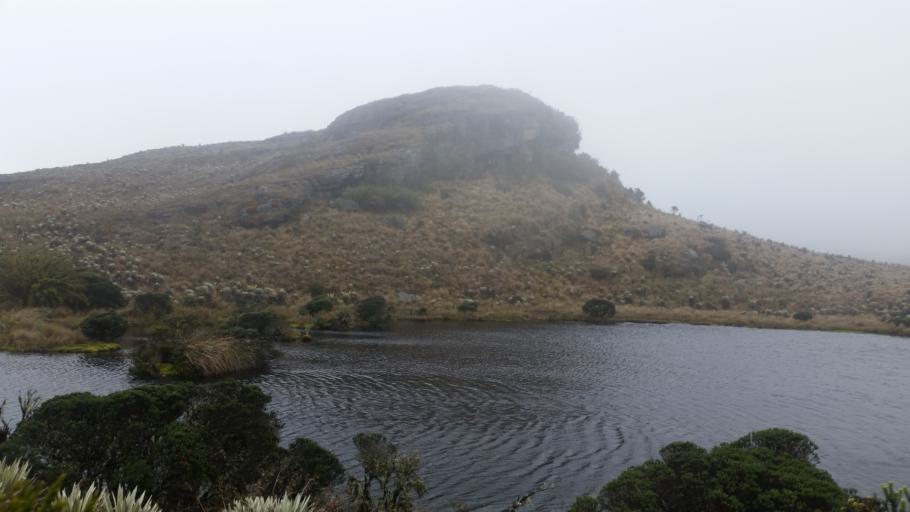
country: CO
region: Cundinamarca
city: Pasca
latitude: 4.3715
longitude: -74.2119
